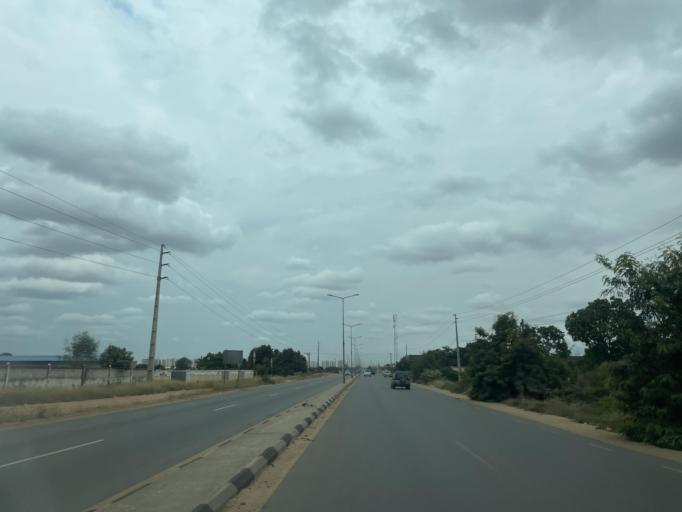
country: AO
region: Luanda
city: Luanda
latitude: -8.9640
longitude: 13.3896
